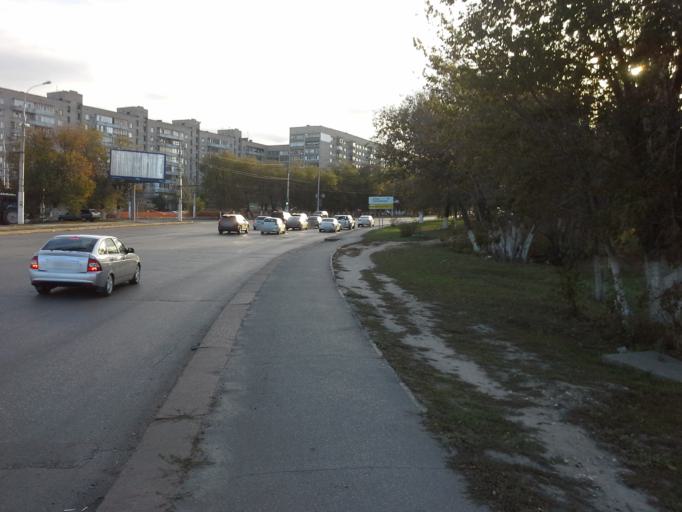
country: RU
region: Volgograd
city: Vodstroy
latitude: 48.8244
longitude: 44.6415
